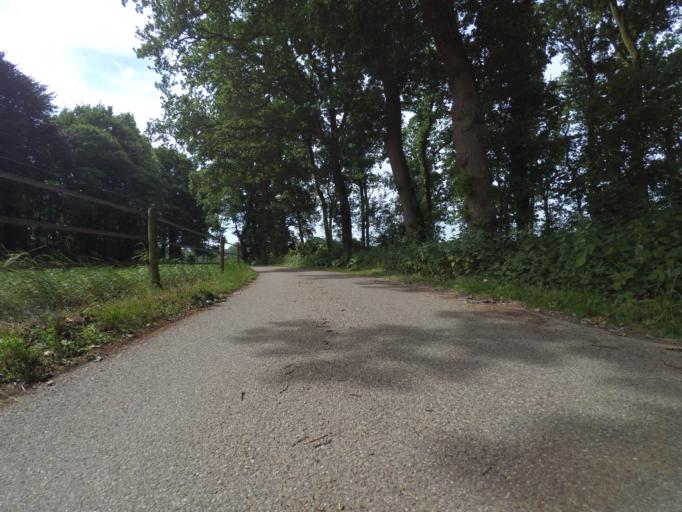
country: NL
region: Utrecht
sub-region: Gemeente Rhenen
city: Rhenen
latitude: 51.9682
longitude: 5.5468
